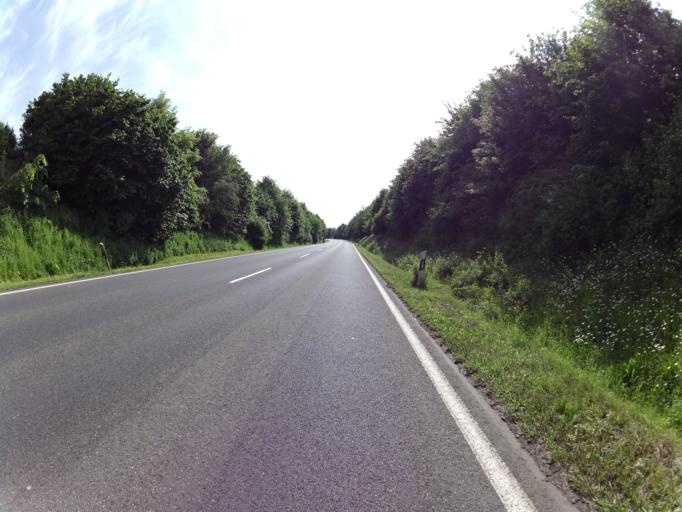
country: DE
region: North Rhine-Westphalia
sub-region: Regierungsbezirk Koln
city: Aldenhoven
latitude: 50.9068
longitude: 6.3226
